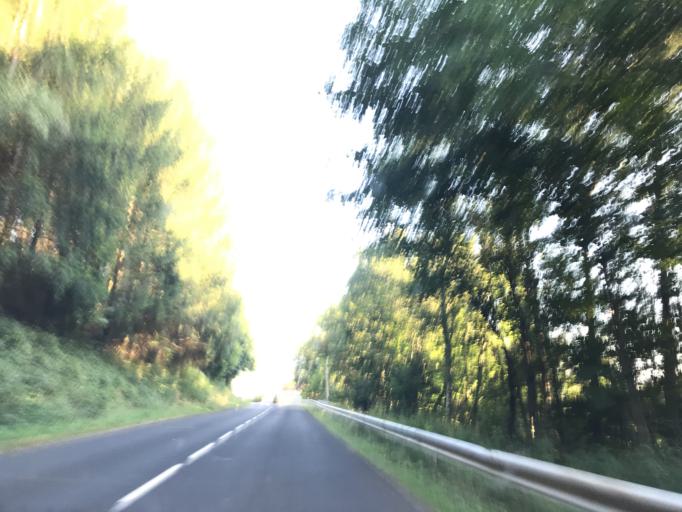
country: FR
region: Auvergne
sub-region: Departement du Puy-de-Dome
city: La Monnerie-le-Montel
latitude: 45.8755
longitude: 3.5989
